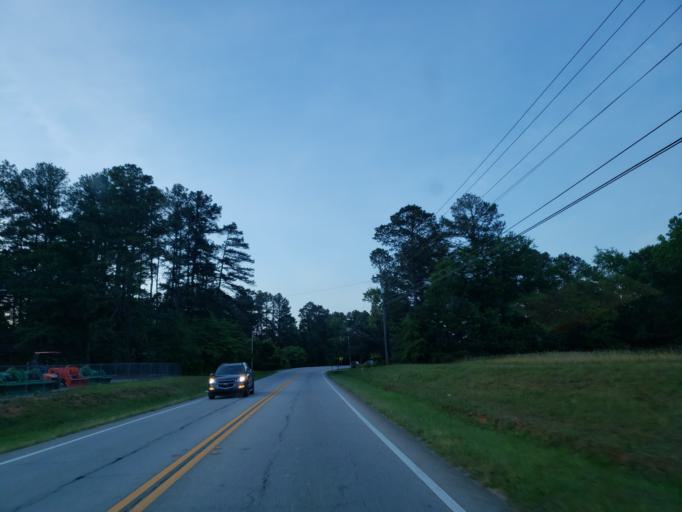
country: US
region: Georgia
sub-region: Douglas County
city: Douglasville
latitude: 33.6782
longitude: -84.8055
